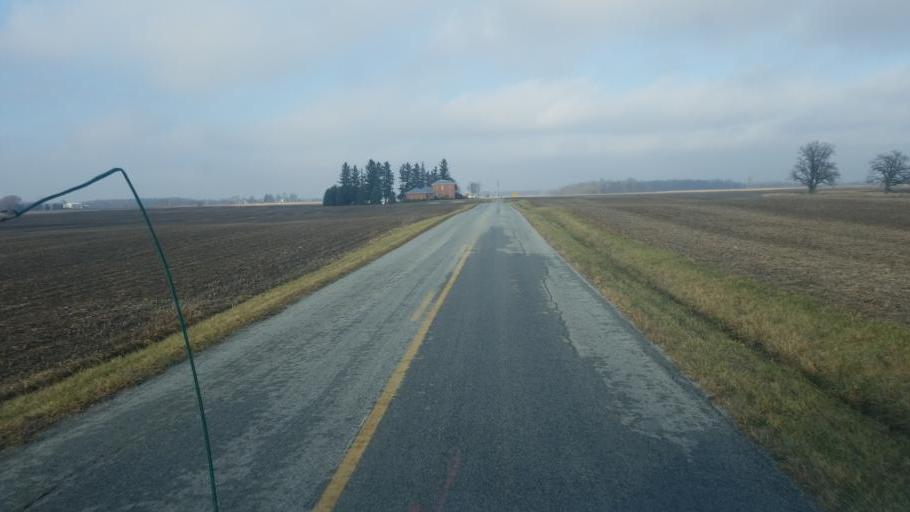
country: US
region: Ohio
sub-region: Hardin County
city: Kenton
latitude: 40.6963
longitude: -83.5931
